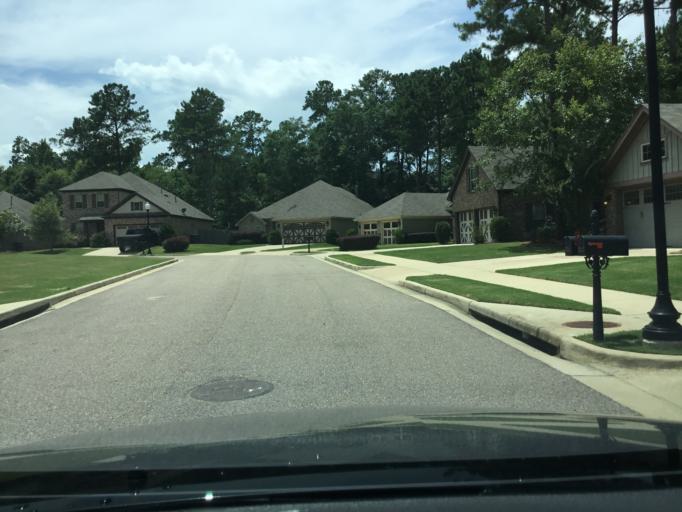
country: US
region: Alabama
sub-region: Montgomery County
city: Pike Road
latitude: 32.3396
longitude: -86.0851
